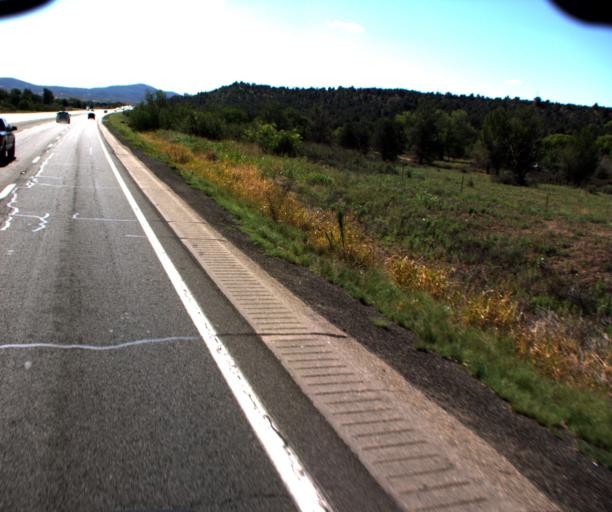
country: US
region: Arizona
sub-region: Yavapai County
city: Dewey-Humboldt
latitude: 34.5715
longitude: -112.2756
